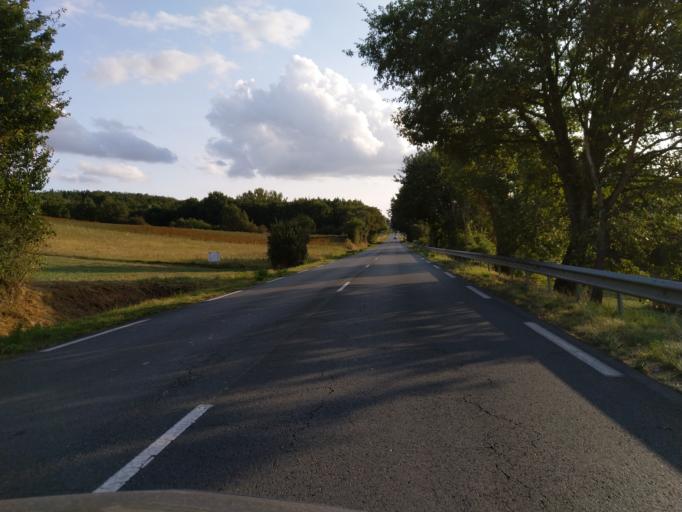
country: FR
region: Midi-Pyrenees
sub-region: Departement du Tarn
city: Realmont
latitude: 43.8239
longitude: 2.1859
